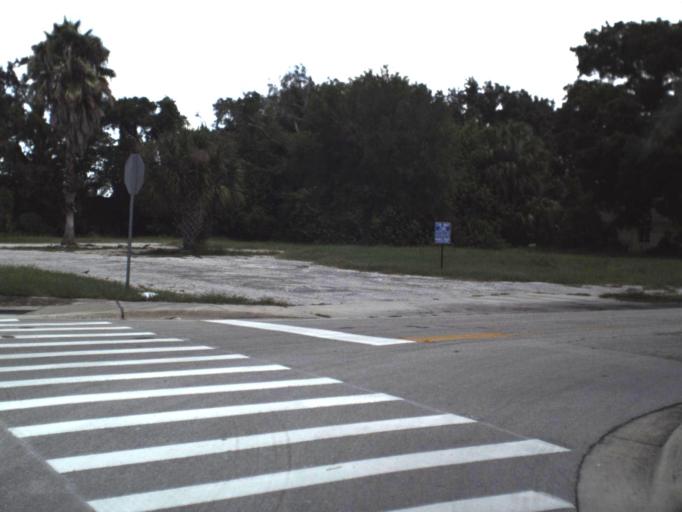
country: US
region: Florida
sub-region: Pinellas County
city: Clearwater
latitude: 27.9744
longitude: -82.7959
